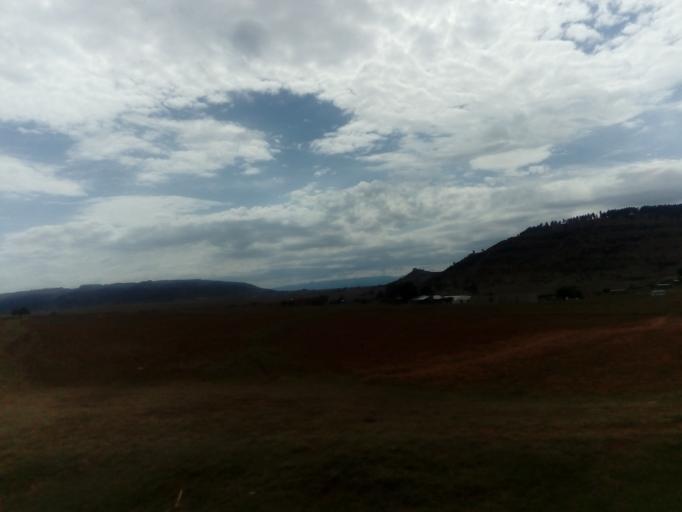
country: LS
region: Leribe
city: Maputsoe
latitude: -28.9474
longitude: 27.9584
